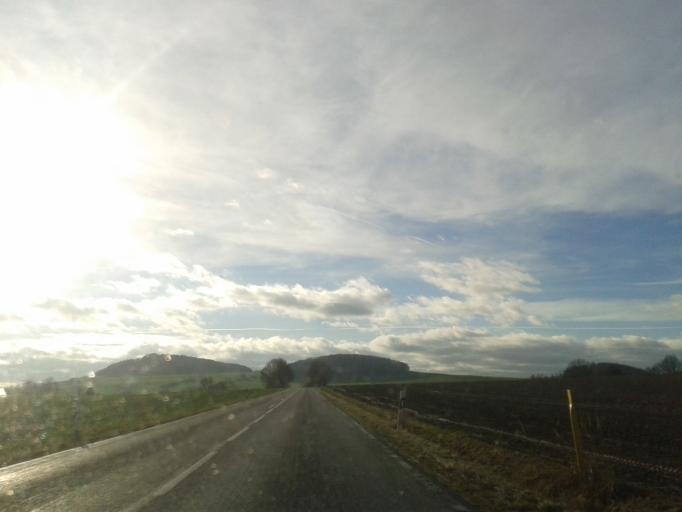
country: DE
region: Saxony
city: Eibau
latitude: 50.9817
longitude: 14.6999
